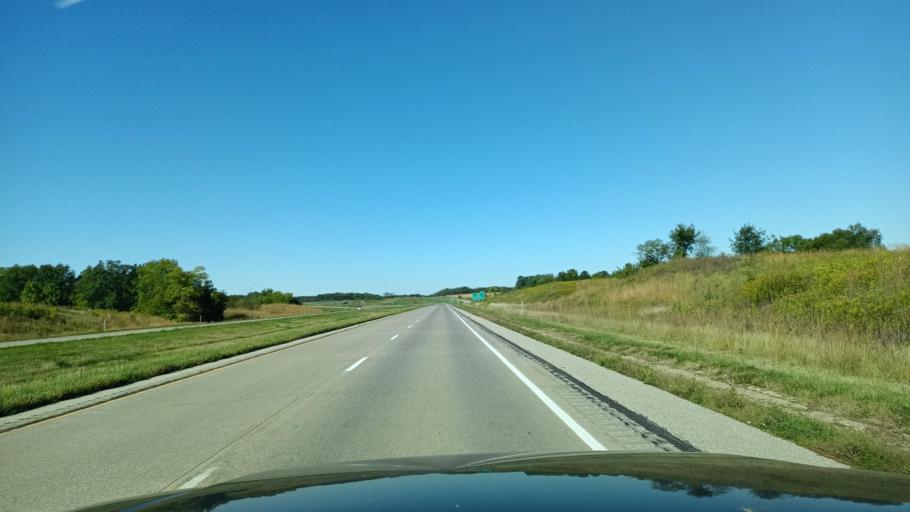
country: US
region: Iowa
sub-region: Lee County
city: Fort Madison
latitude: 40.6706
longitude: -91.3464
